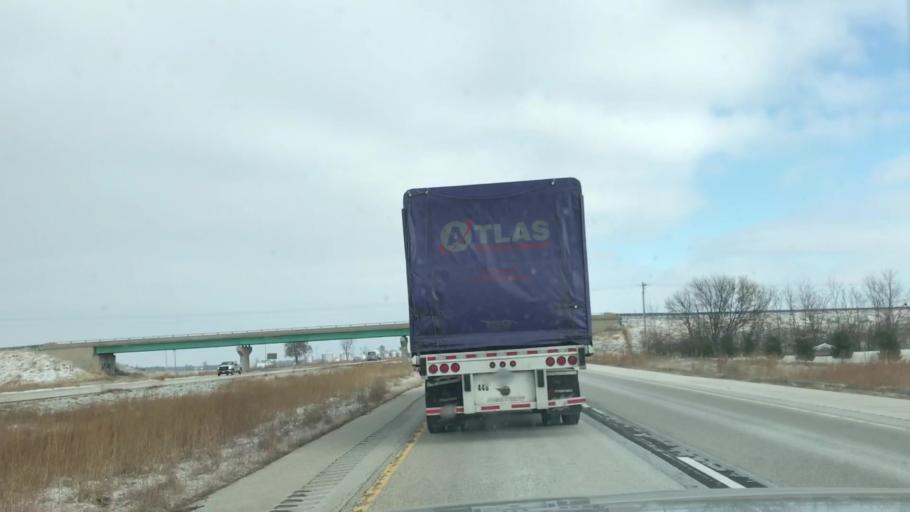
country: US
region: Illinois
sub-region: Sangamon County
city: Divernon
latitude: 39.5227
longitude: -89.6455
